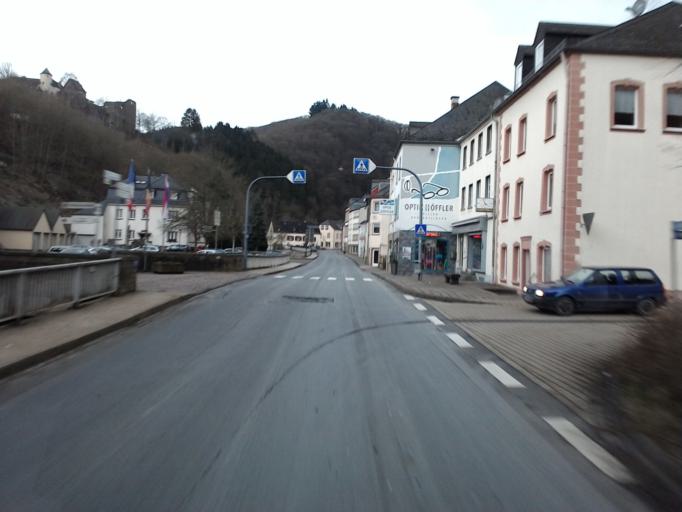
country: DE
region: Rheinland-Pfalz
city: Scheuern
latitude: 50.0115
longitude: 6.2947
